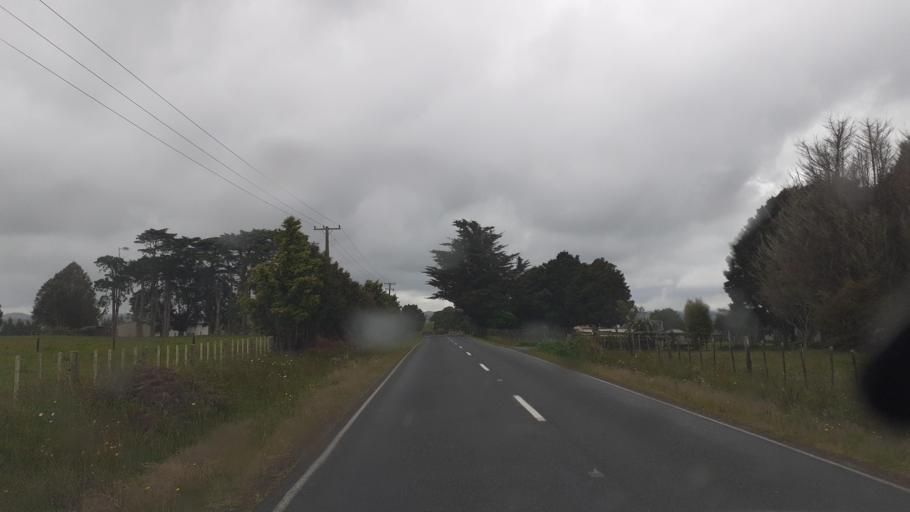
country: NZ
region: Northland
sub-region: Far North District
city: Waimate North
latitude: -35.2776
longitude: 173.8307
